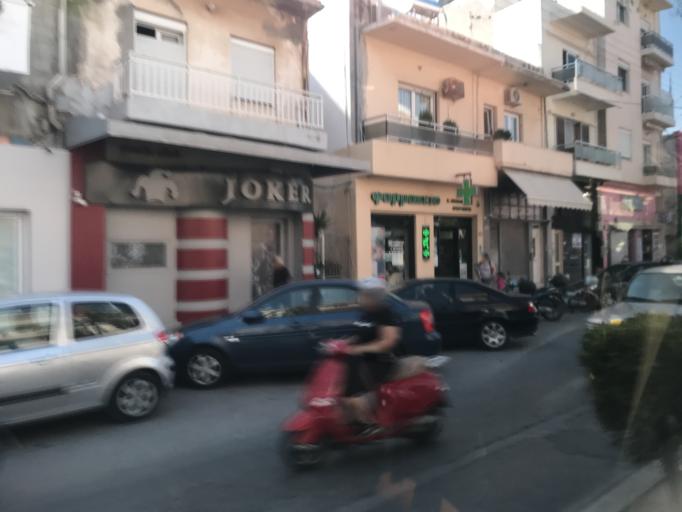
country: GR
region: Crete
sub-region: Nomos Irakleiou
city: Irakleion
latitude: 35.3359
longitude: 25.1196
